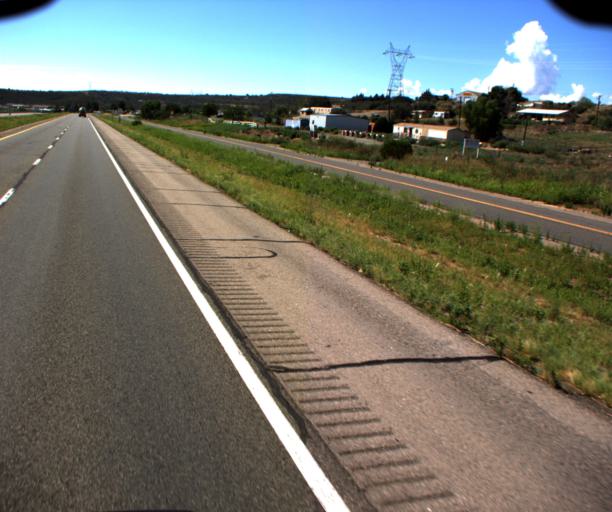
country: US
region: Arizona
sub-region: Yavapai County
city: Mayer
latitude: 34.3925
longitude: -112.2220
